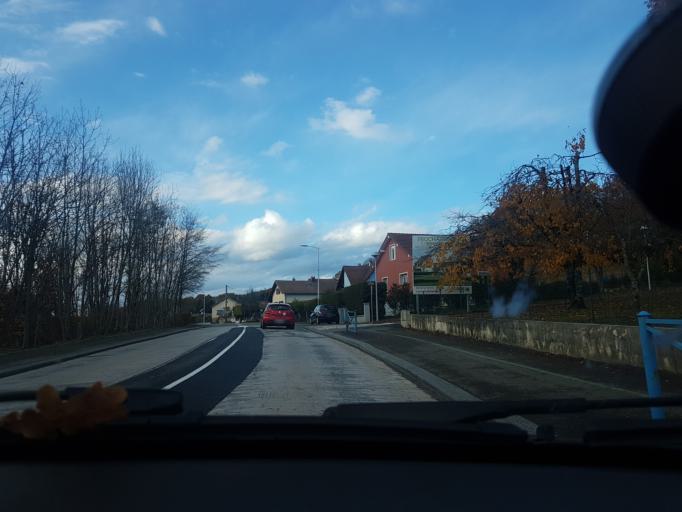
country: FR
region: Franche-Comte
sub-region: Territoire de Belfort
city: Essert
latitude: 47.6380
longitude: 6.8040
